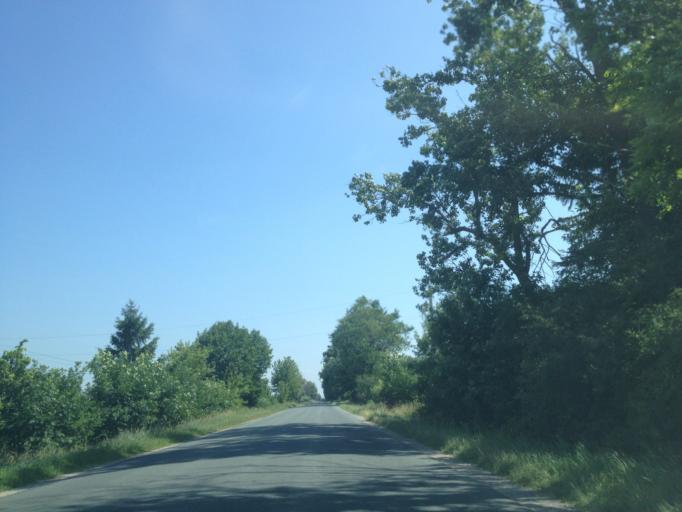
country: CA
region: Ontario
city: London
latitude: 43.2587
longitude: -81.2048
